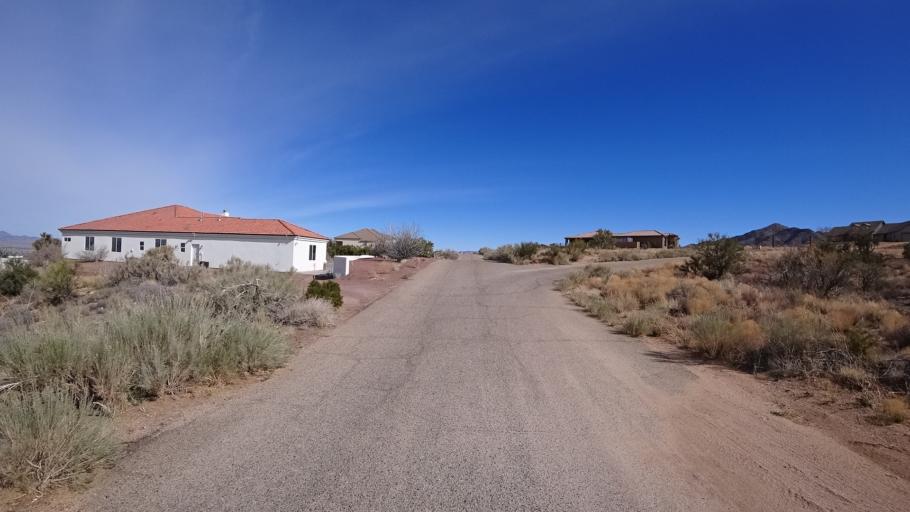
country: US
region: Arizona
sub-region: Mohave County
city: Kingman
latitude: 35.1712
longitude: -113.9782
